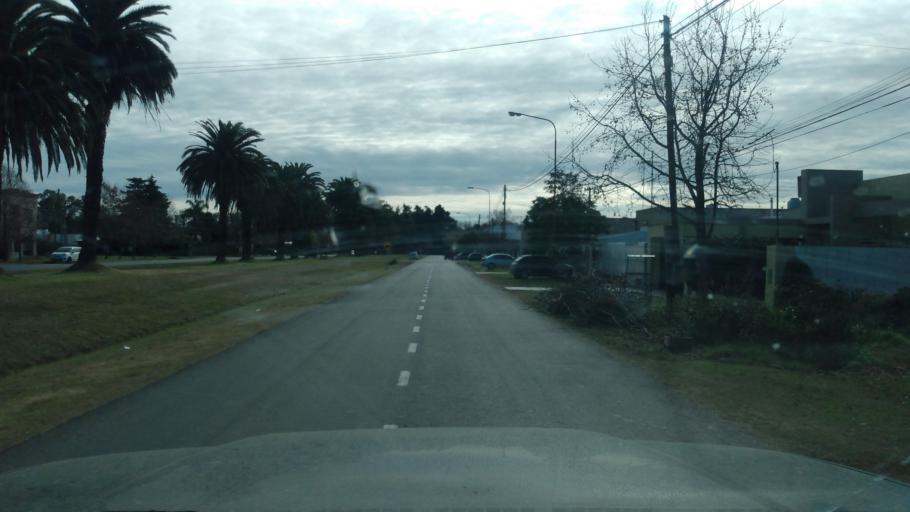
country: AR
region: Buenos Aires
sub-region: Partido de Lujan
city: Lujan
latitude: -34.5952
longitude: -59.1776
